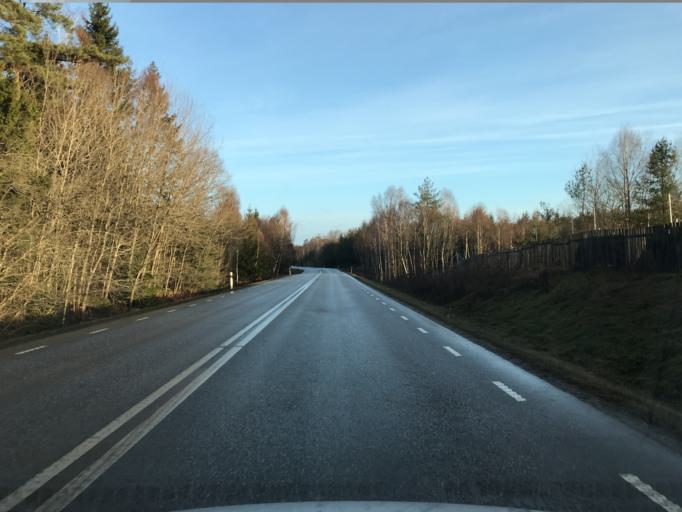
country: SE
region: Skane
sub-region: Hassleholms Kommun
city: Bjarnum
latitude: 56.2517
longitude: 13.7170
